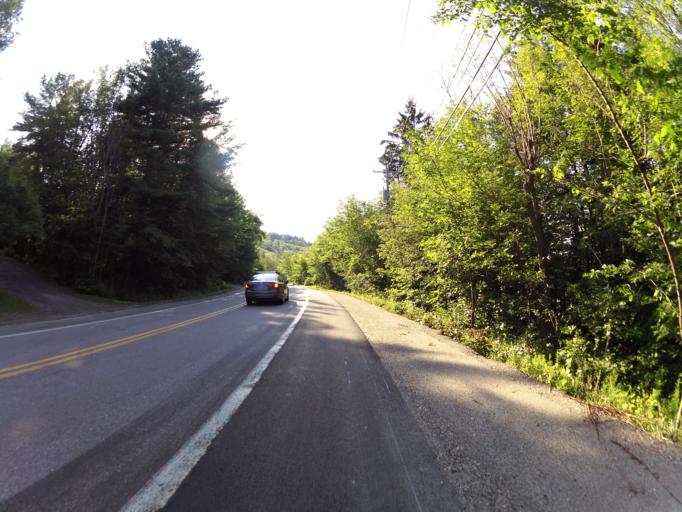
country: CA
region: Quebec
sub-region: Outaouais
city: Wakefield
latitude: 45.5593
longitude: -75.8367
